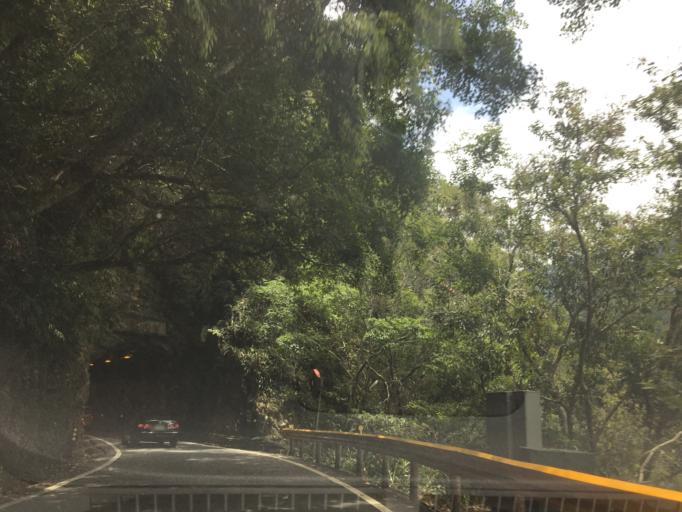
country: TW
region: Taiwan
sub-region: Hualien
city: Hualian
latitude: 24.1920
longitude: 121.4810
